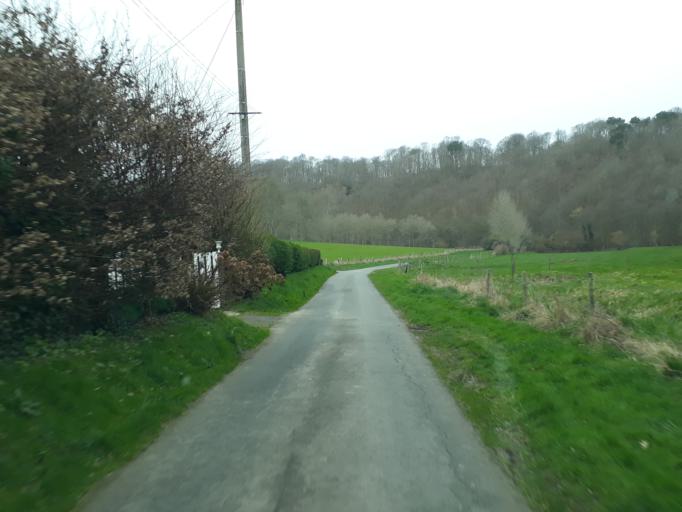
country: FR
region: Haute-Normandie
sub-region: Departement de la Seine-Maritime
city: Les Loges
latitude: 49.6736
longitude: 0.2653
